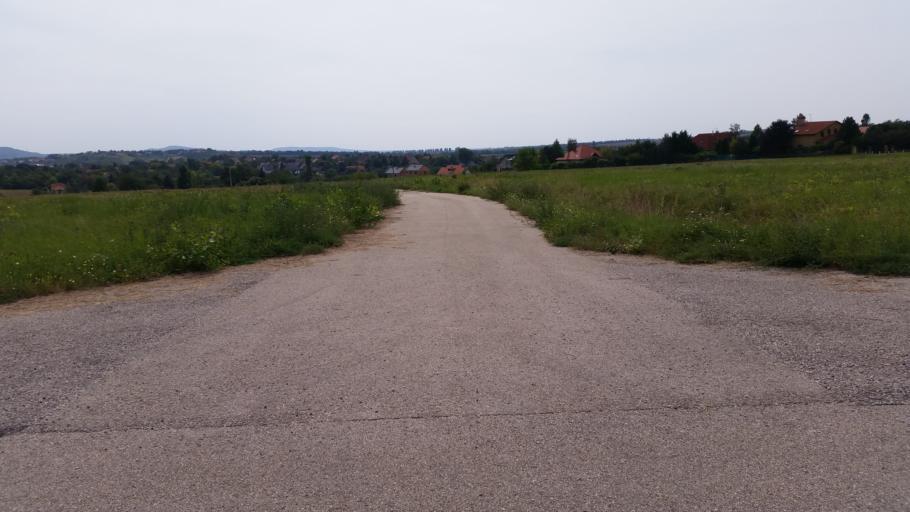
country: HU
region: Pest
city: Telki
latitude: 47.5609
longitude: 18.8117
